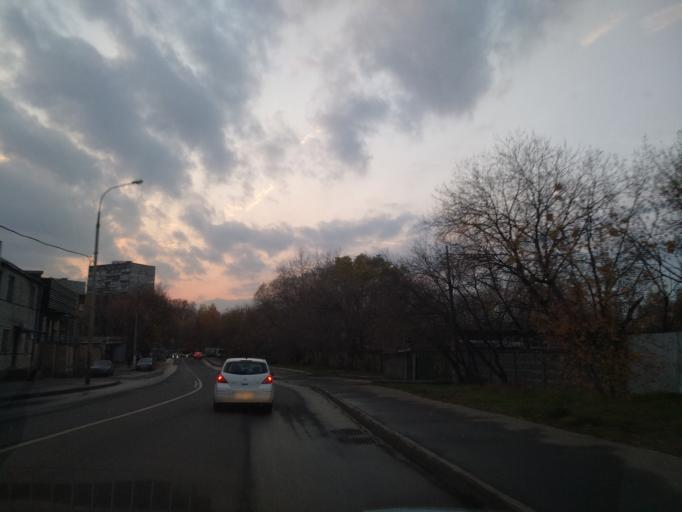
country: RU
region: Moscow
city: Leonovo
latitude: 55.8638
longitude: 37.6474
